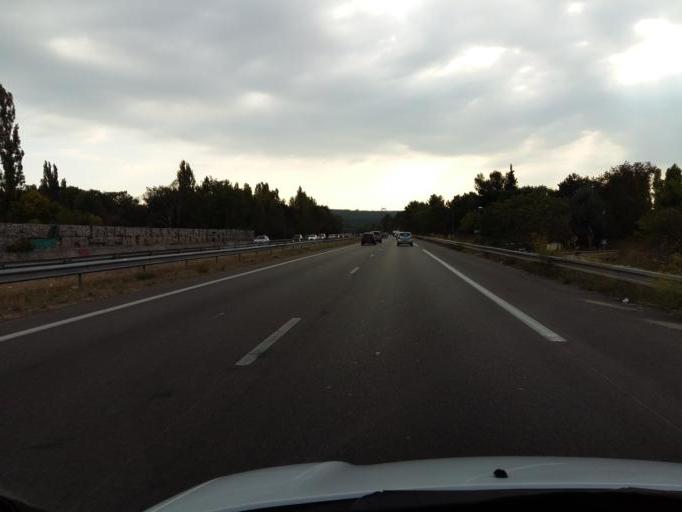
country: FR
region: Provence-Alpes-Cote d'Azur
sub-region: Departement des Bouches-du-Rhone
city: Bouc-Bel-Air
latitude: 43.4583
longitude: 5.4019
